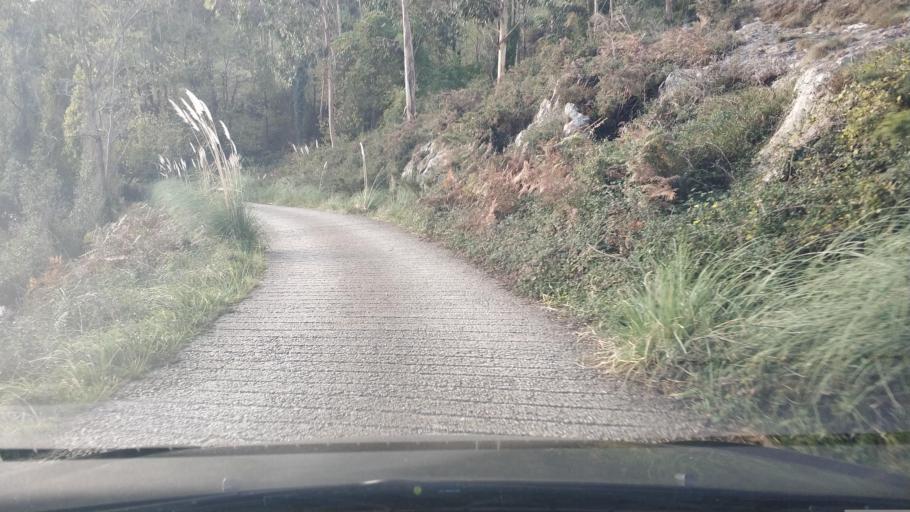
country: ES
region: Cantabria
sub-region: Provincia de Cantabria
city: Luzmela
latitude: 43.3392
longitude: -4.1862
